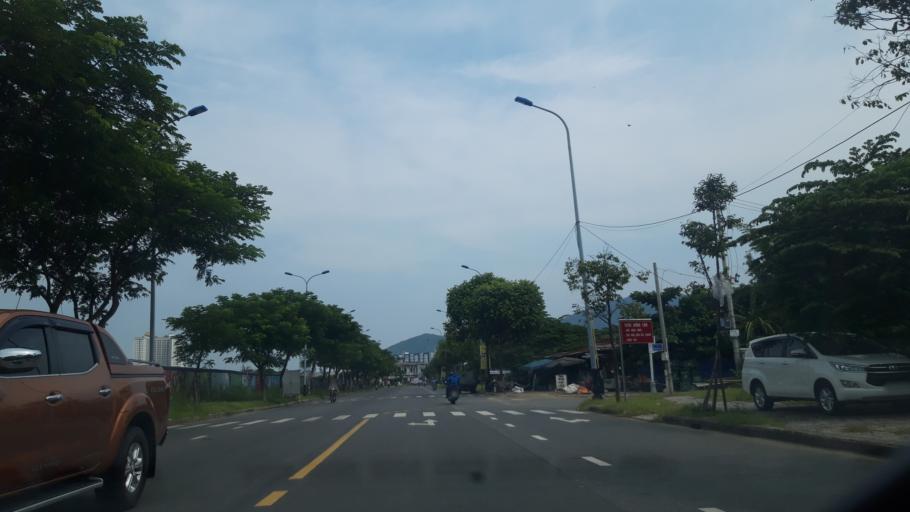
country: VN
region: Da Nang
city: Da Nang
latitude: 16.0861
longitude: 108.2289
